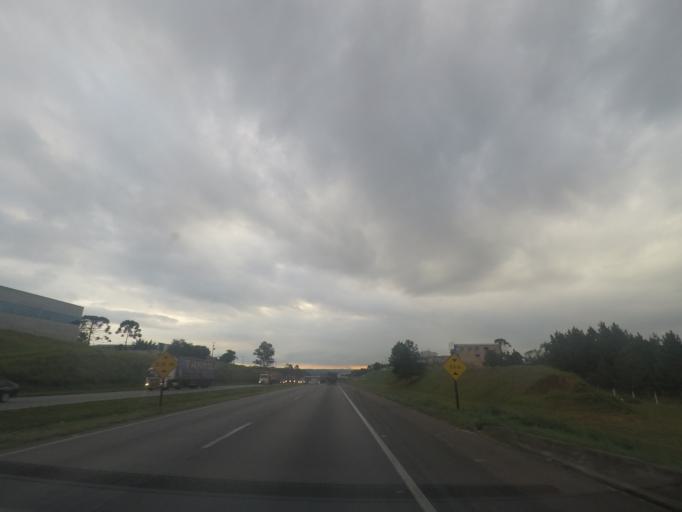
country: BR
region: Parana
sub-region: Sao Jose Dos Pinhais
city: Sao Jose dos Pinhais
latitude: -25.5707
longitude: -49.2136
